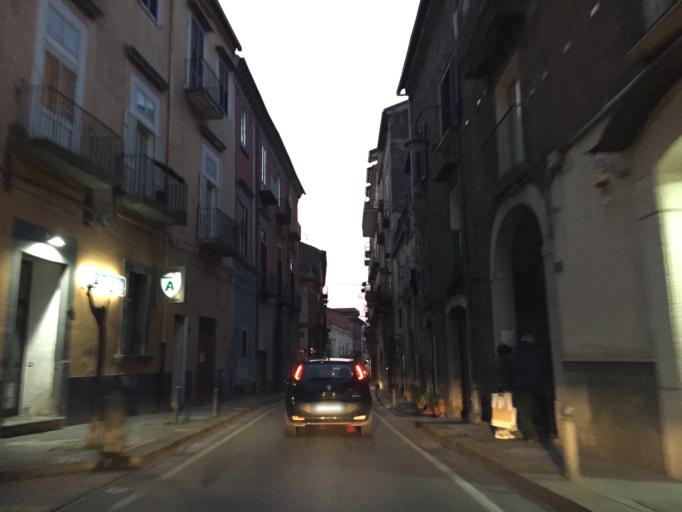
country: IT
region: Campania
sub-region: Provincia di Salerno
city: Nocera Inferiore
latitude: 40.7474
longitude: 14.6406
